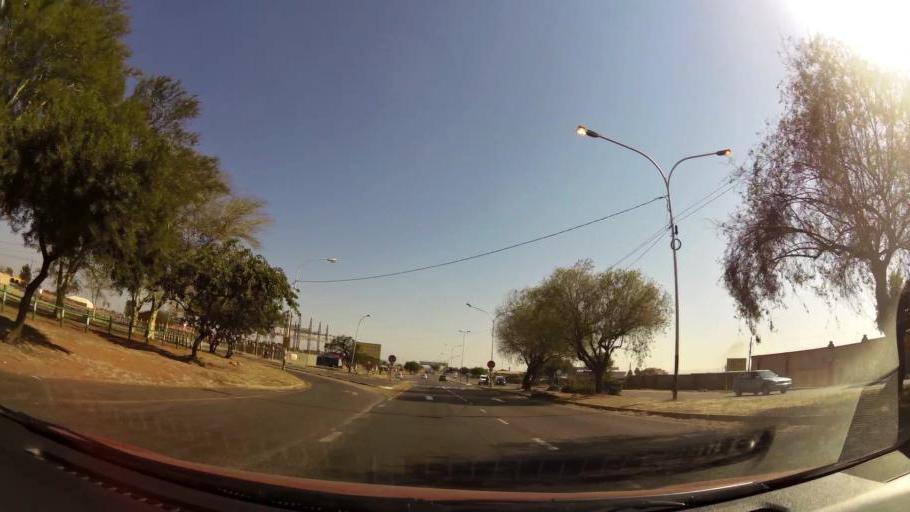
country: ZA
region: Gauteng
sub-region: City of Tshwane Metropolitan Municipality
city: Mabopane
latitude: -25.5228
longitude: 28.0967
